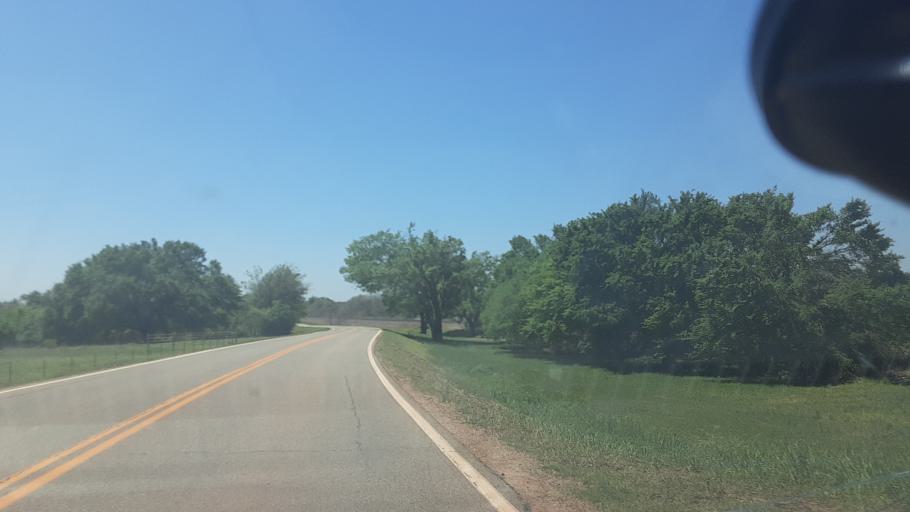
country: US
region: Oklahoma
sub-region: Logan County
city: Langston
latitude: 36.0817
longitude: -97.3994
